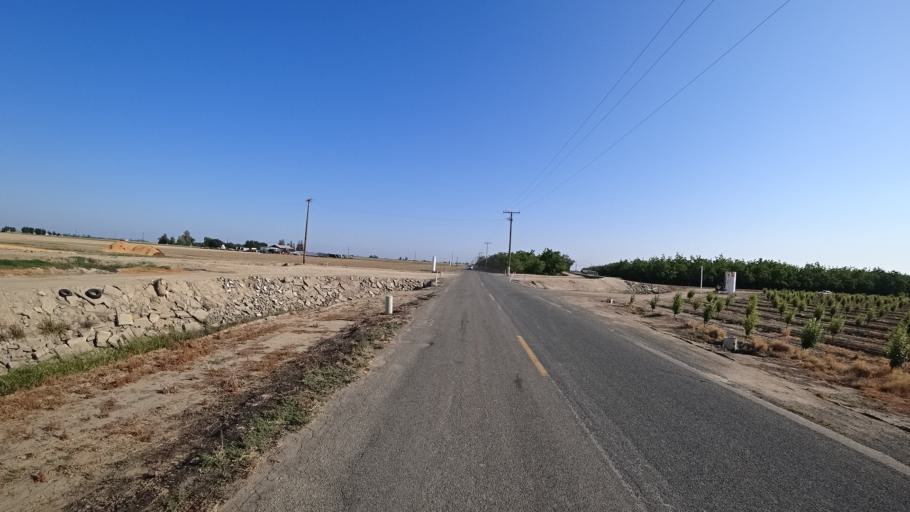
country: US
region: California
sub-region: Kings County
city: Home Garden
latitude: 36.2943
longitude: -119.5652
